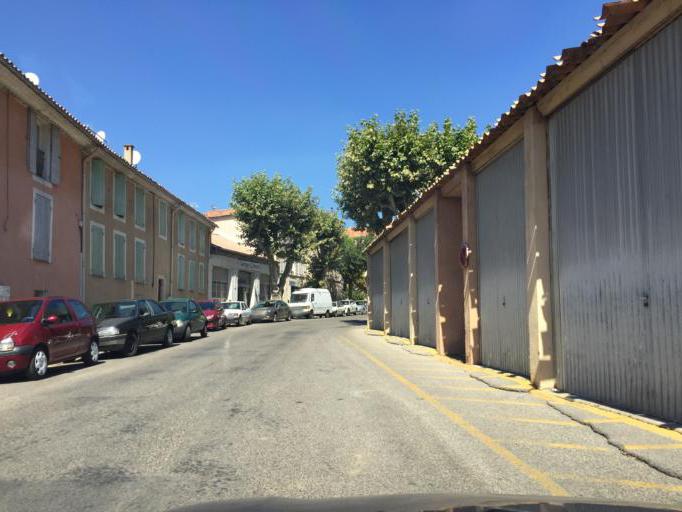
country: FR
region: Provence-Alpes-Cote d'Azur
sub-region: Departement des Alpes-de-Haute-Provence
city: Forcalquier
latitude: 43.9570
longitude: 5.7793
